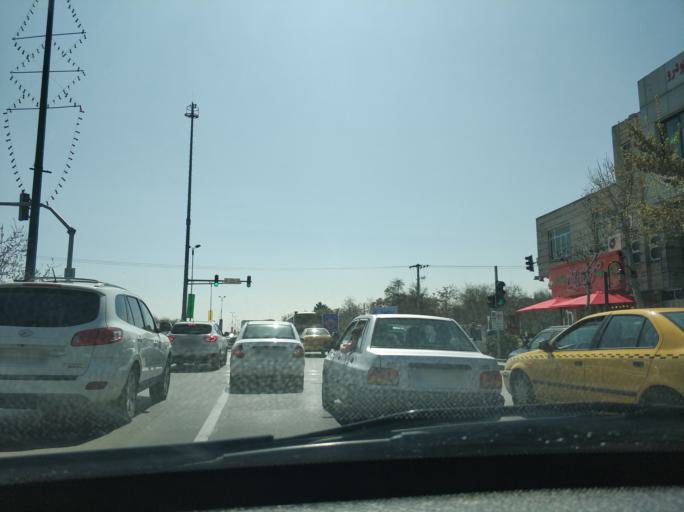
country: IR
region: Razavi Khorasan
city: Mashhad
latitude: 36.2580
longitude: 59.6086
